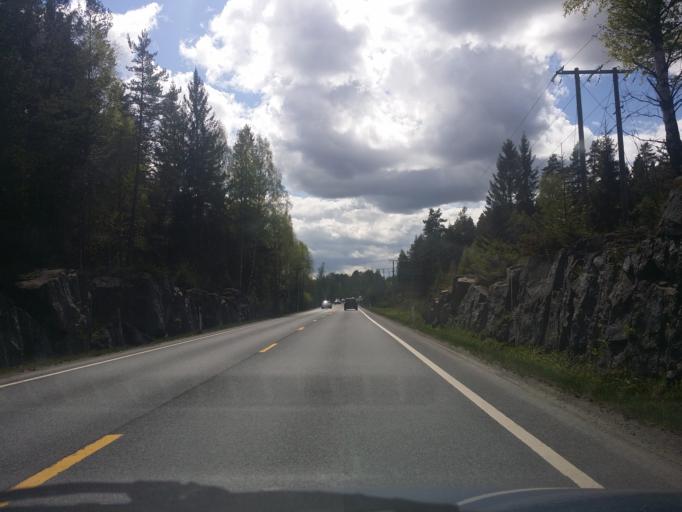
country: NO
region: Buskerud
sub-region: Modum
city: Vikersund
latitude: 59.9545
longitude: 9.9755
